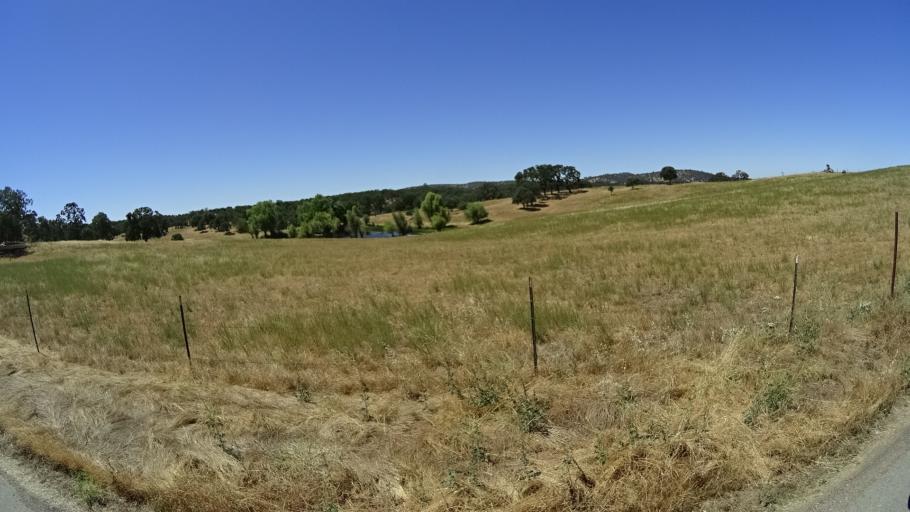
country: US
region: California
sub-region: Calaveras County
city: Copperopolis
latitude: 38.0355
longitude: -120.7234
